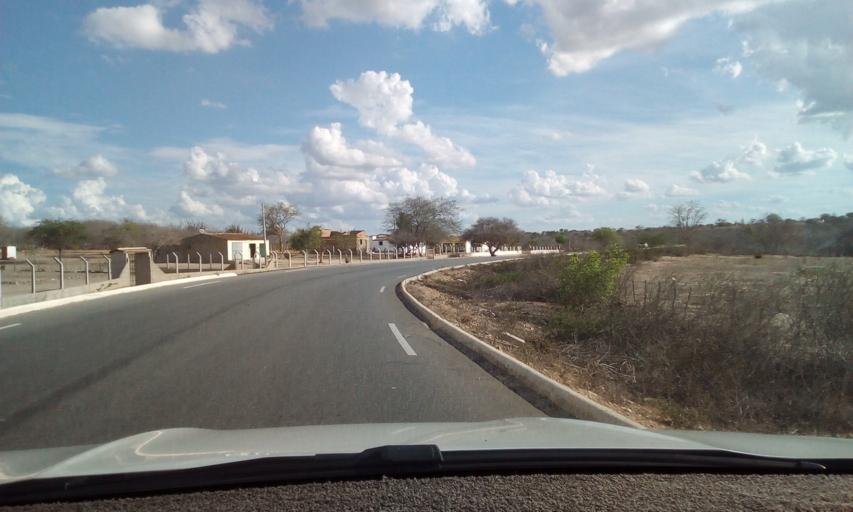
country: BR
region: Paraiba
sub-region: Soledade
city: Soledade
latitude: -6.9124
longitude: -36.3855
